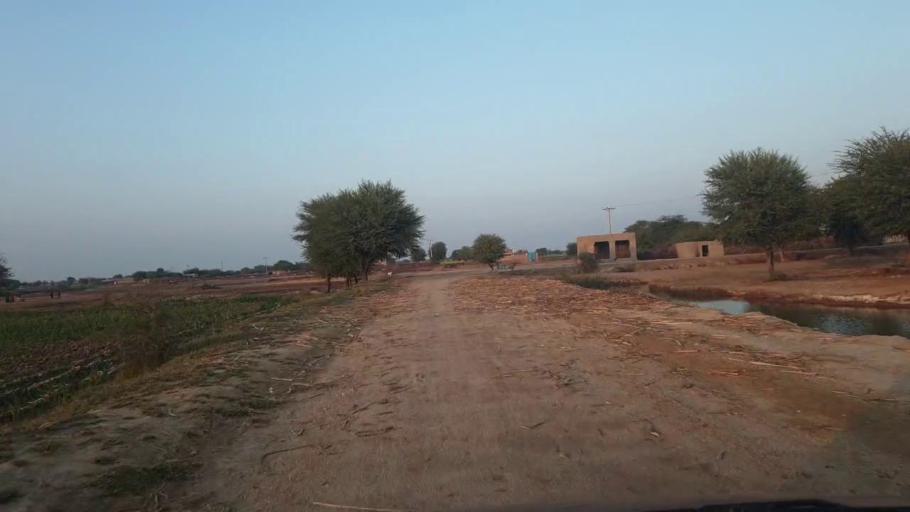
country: PK
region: Sindh
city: Berani
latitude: 25.8290
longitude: 68.7472
